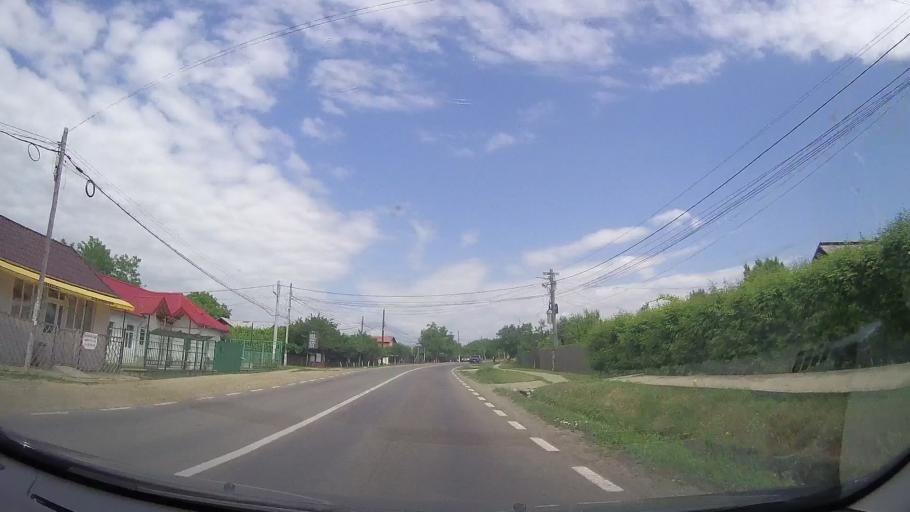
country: RO
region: Prahova
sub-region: Comuna Magurele
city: Magurele
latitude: 45.1144
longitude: 26.0344
